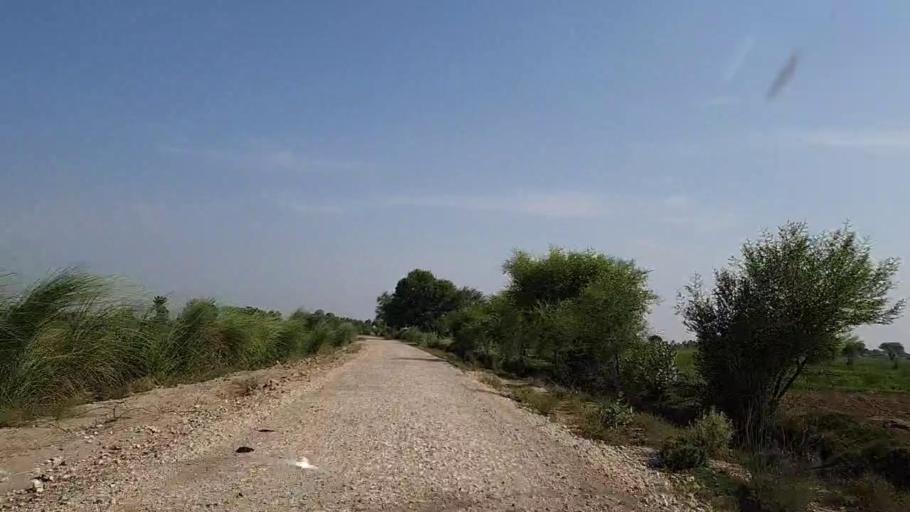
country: PK
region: Sindh
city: Khanpur
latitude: 27.7039
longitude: 69.3632
